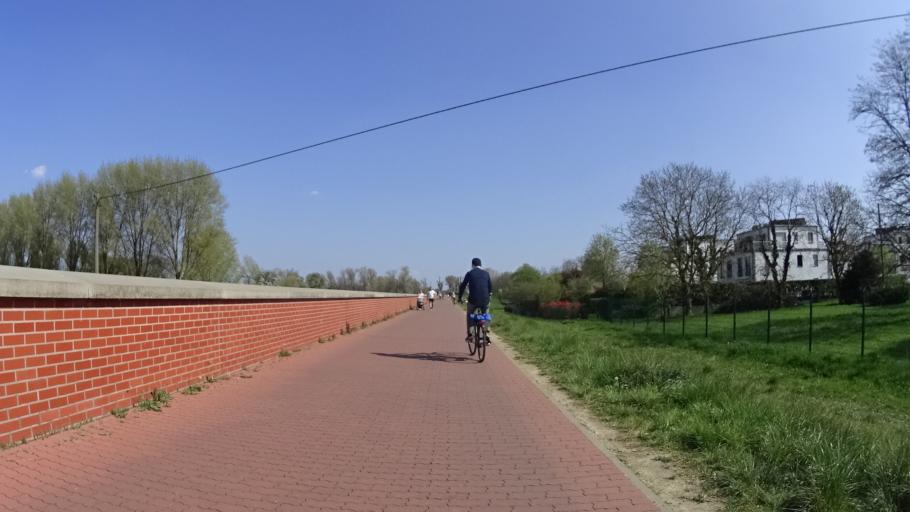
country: DE
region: North Rhine-Westphalia
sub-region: Regierungsbezirk Dusseldorf
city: Meerbusch
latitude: 51.2548
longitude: 6.7169
